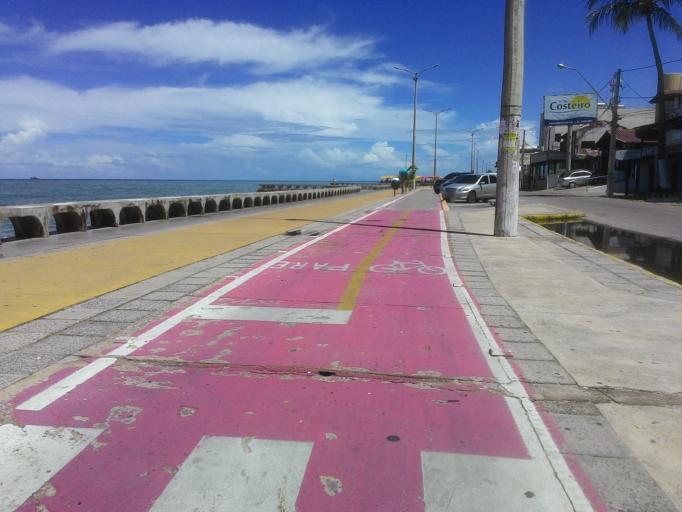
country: BR
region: Pernambuco
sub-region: Olinda
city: Olinda
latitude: -8.0055
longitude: -34.8402
